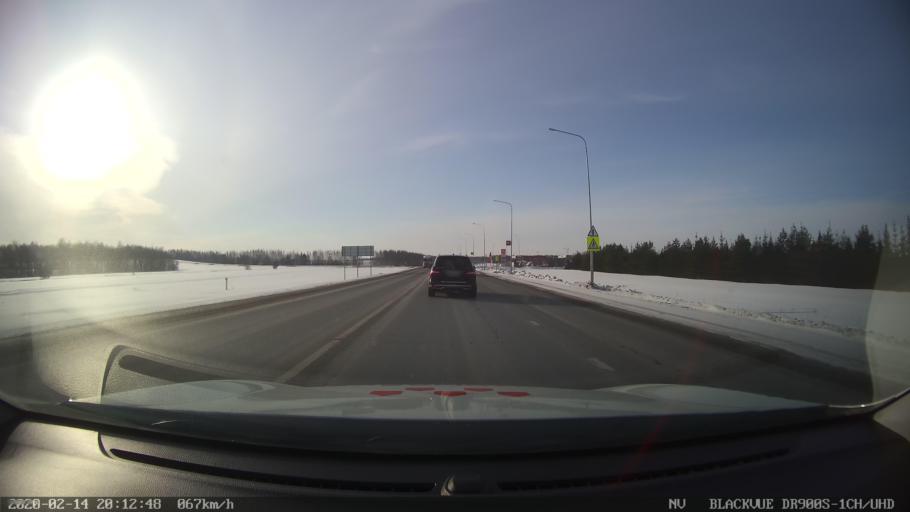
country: RU
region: Tatarstan
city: Verkhniy Uslon
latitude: 55.6622
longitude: 48.8595
